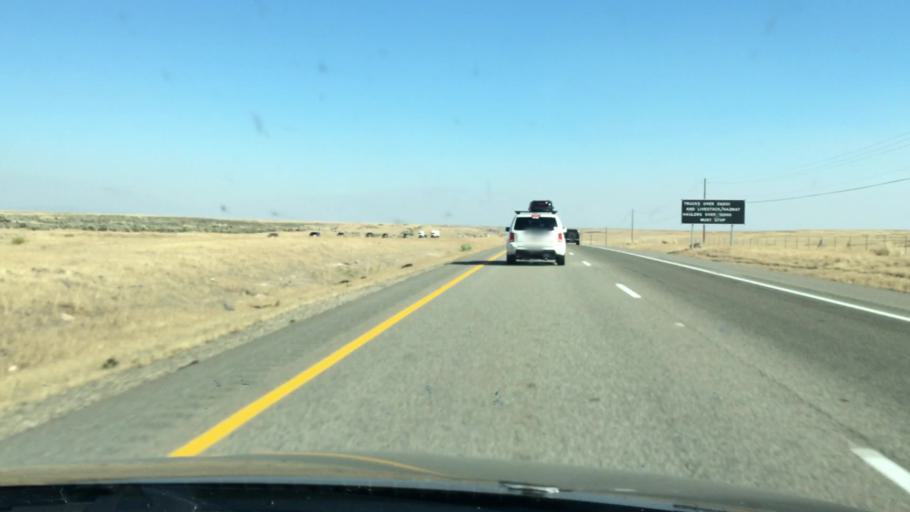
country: US
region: Idaho
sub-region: Ada County
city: Boise
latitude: 43.4515
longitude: -116.0801
